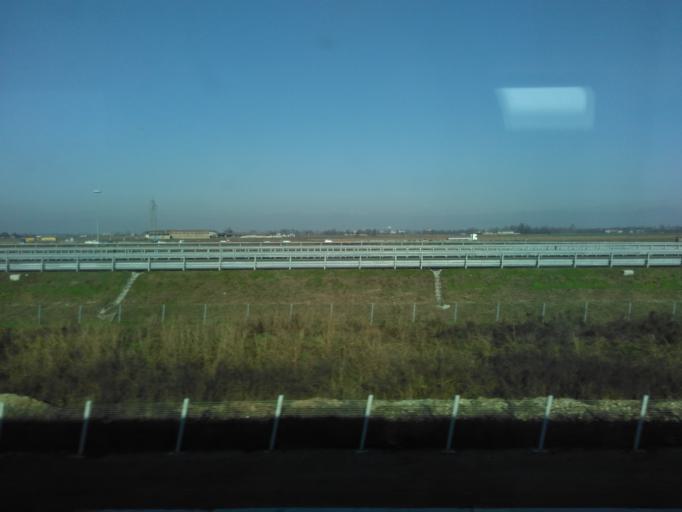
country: IT
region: Lombardy
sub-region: Provincia di Bergamo
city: Antegnate
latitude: 45.4953
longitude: 9.8165
